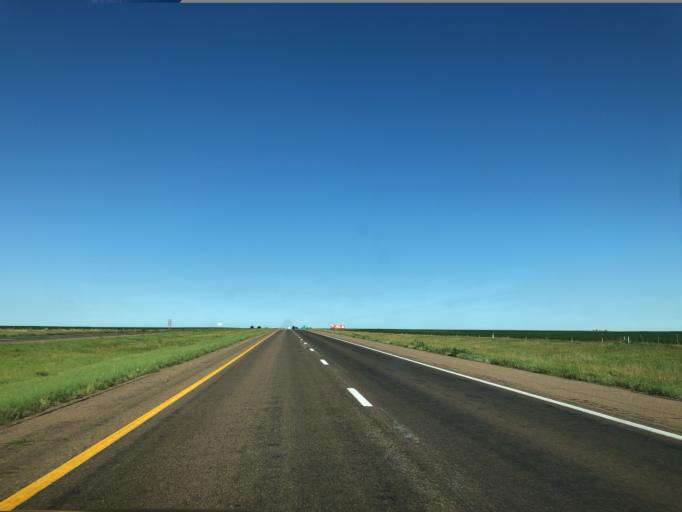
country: US
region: Kansas
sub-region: Thomas County
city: Colby
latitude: 39.3660
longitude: -101.1844
